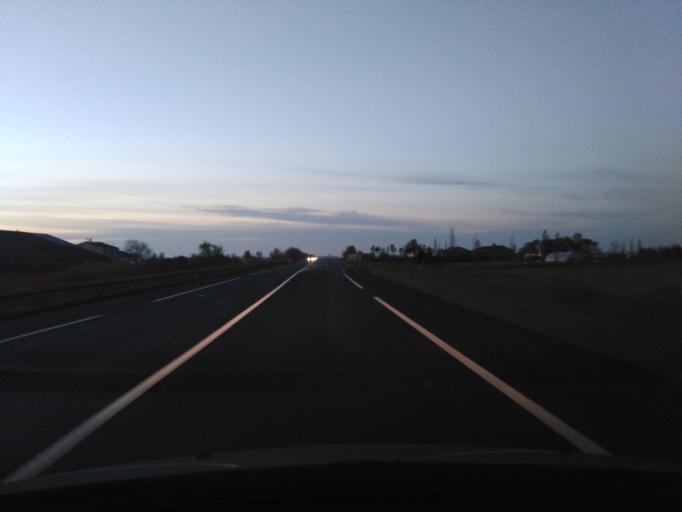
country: FR
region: Pays de la Loire
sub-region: Departement de la Vendee
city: Champagne-les-Marais
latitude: 46.4014
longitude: -1.0965
